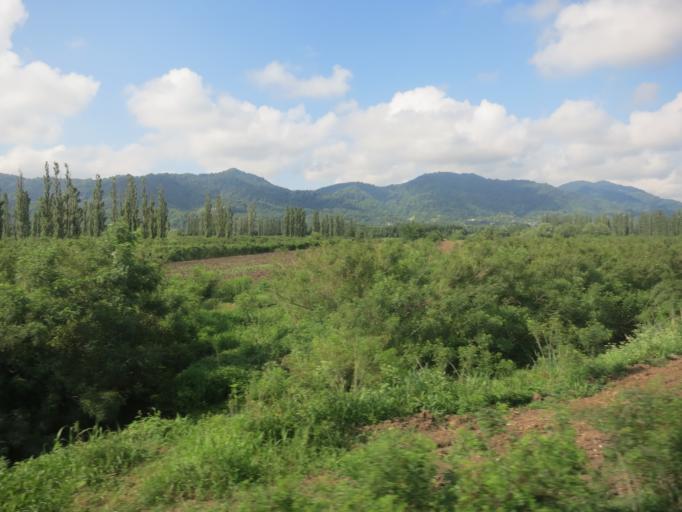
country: GE
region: Guria
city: Lanchkhuti
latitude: 42.0857
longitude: 42.0672
